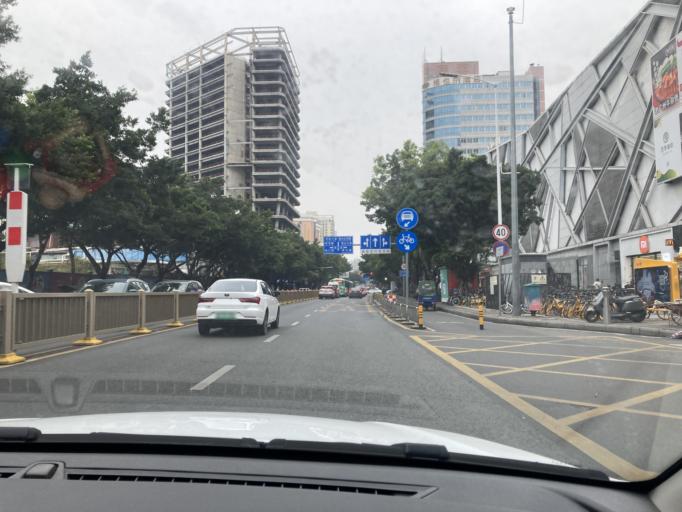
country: CN
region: Guangdong
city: Nantou
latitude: 22.5376
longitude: 113.9145
